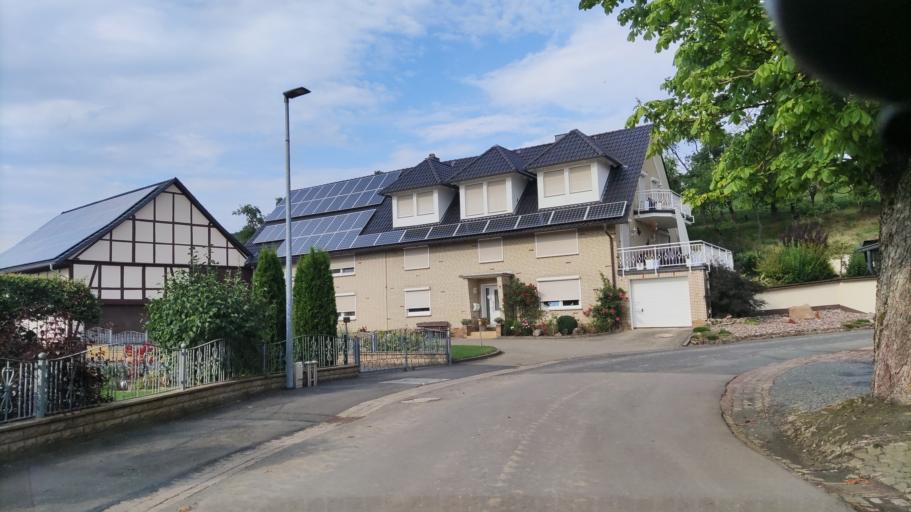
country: DE
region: Lower Saxony
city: Eimen
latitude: 51.8337
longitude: 9.7994
